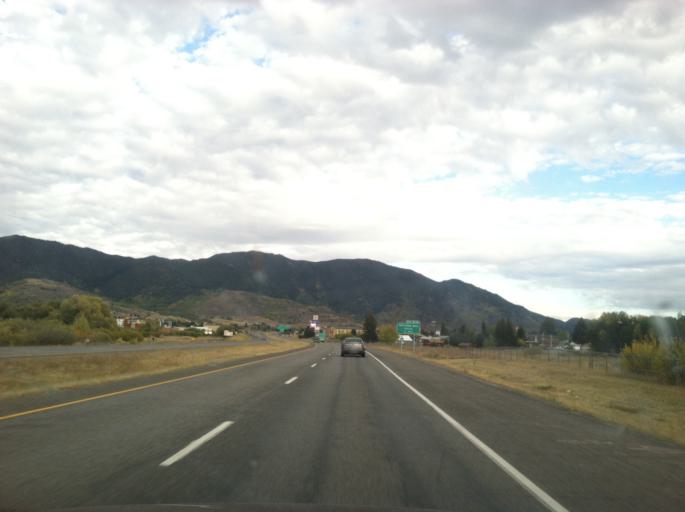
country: US
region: Montana
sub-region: Silver Bow County
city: Butte
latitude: 45.9875
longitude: -112.5191
